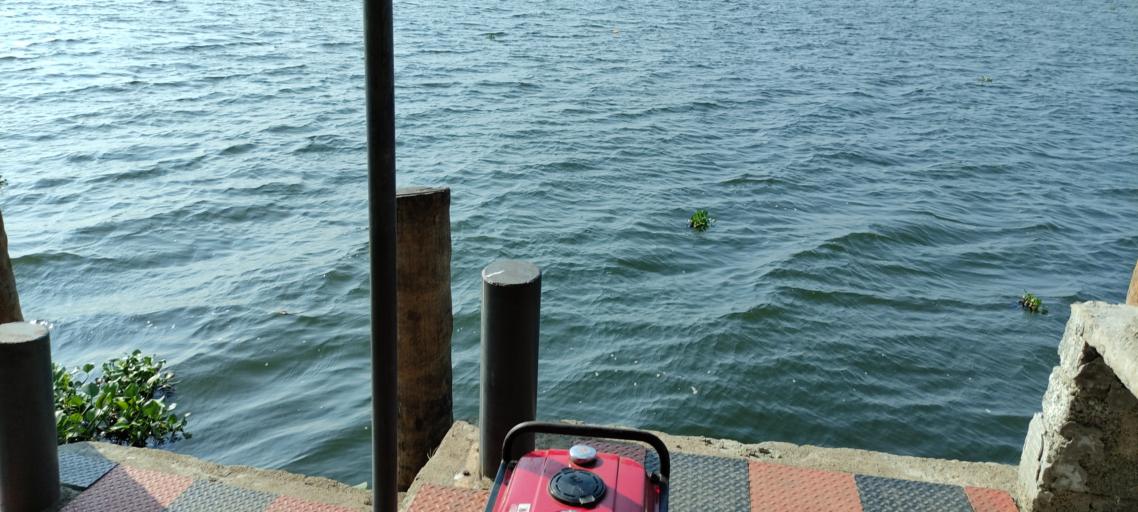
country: IN
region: Kerala
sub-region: Alappuzha
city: Shertallai
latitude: 9.6198
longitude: 76.3830
